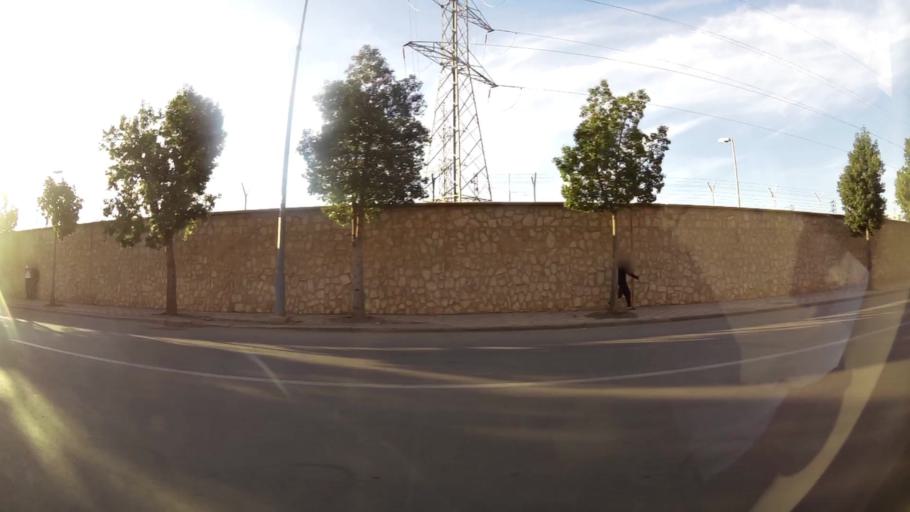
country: MA
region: Oriental
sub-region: Oujda-Angad
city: Oujda
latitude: 34.7031
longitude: -1.9183
